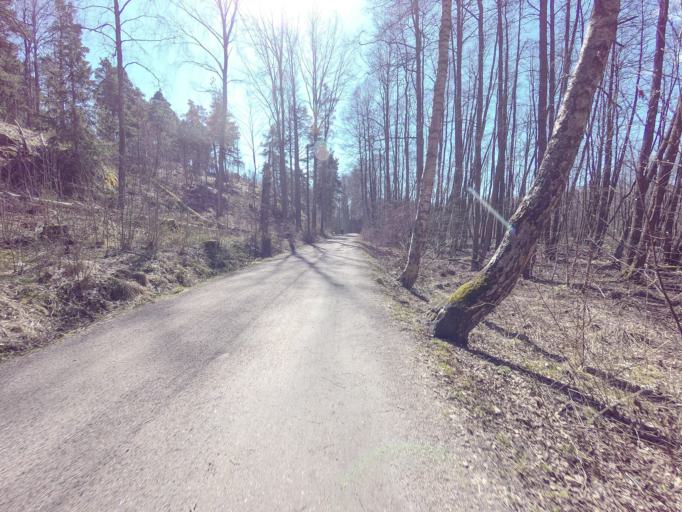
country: FI
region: Uusimaa
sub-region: Helsinki
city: Vantaa
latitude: 60.2082
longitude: 25.0282
